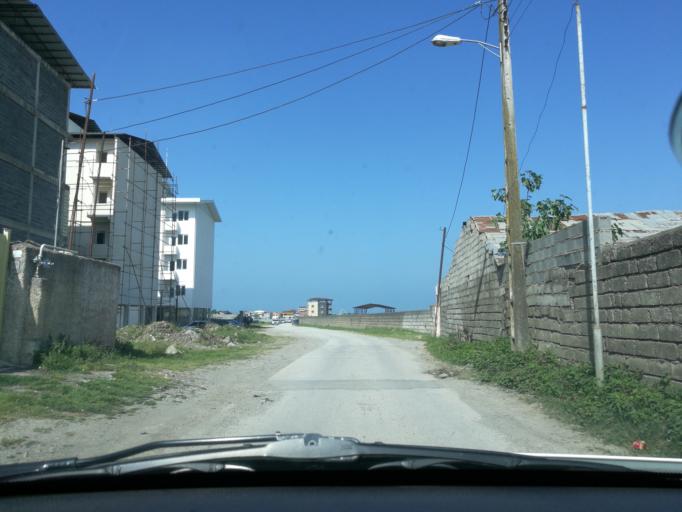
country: IR
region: Mazandaran
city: Chalus
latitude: 36.6634
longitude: 51.4409
